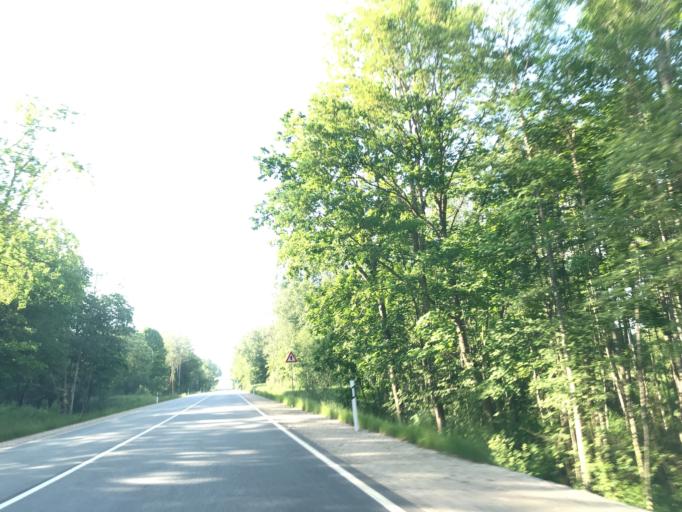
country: LV
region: Lielvarde
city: Lielvarde
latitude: 56.6555
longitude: 24.8763
